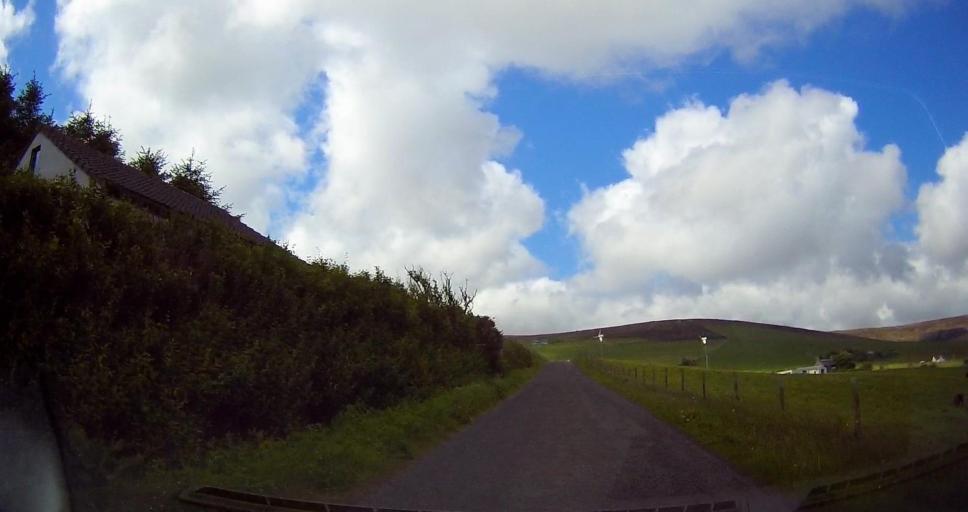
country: GB
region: Scotland
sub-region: Orkney Islands
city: Orkney
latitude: 59.0487
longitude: -3.1009
